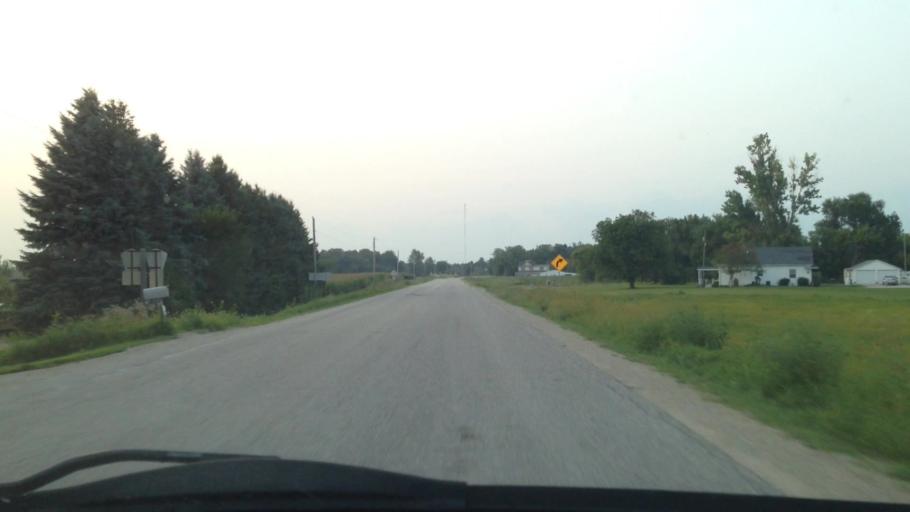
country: US
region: Iowa
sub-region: Benton County
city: Urbana
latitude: 42.1390
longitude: -91.8769
